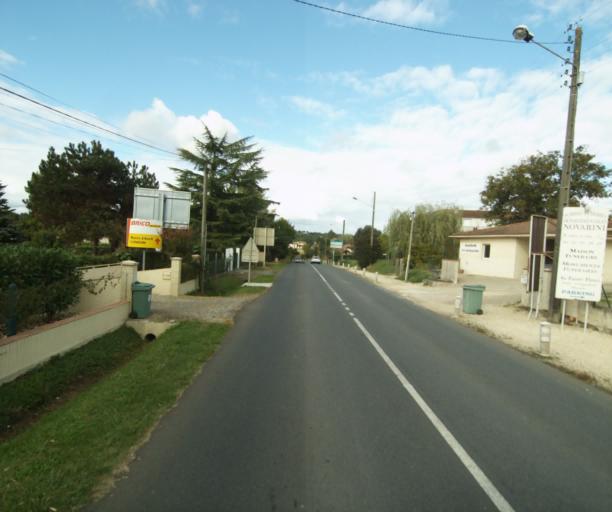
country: FR
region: Midi-Pyrenees
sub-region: Departement du Gers
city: Eauze
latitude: 43.8643
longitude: 0.1082
